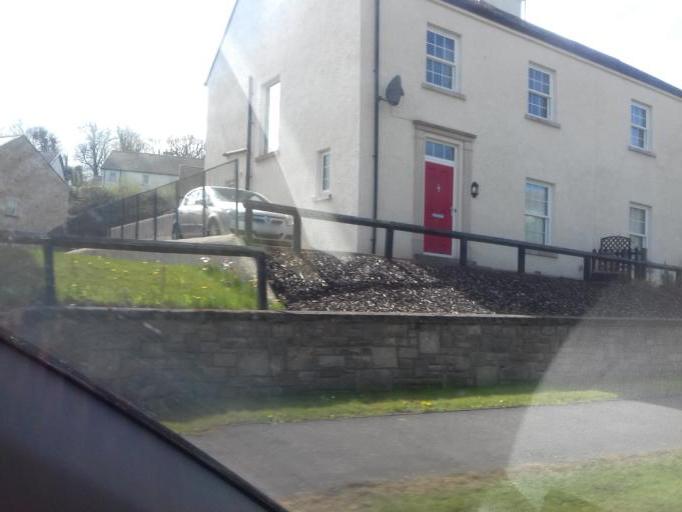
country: GB
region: Northern Ireland
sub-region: Fermanagh District
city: Enniskillen
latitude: 54.3614
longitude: -7.6760
